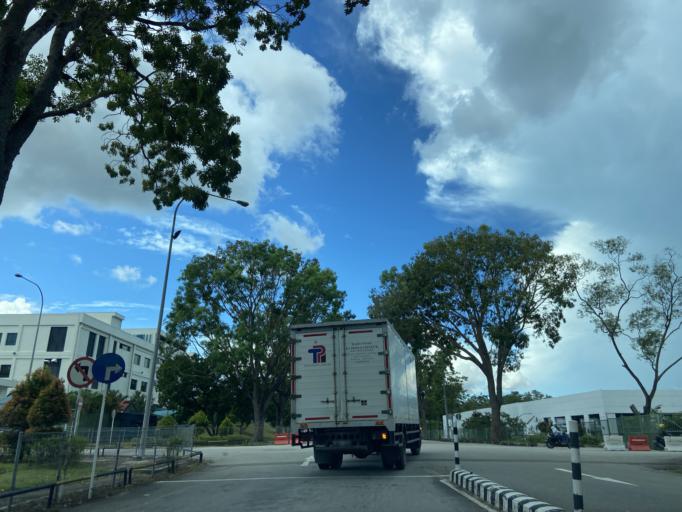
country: SG
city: Singapore
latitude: 1.0646
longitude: 104.0314
